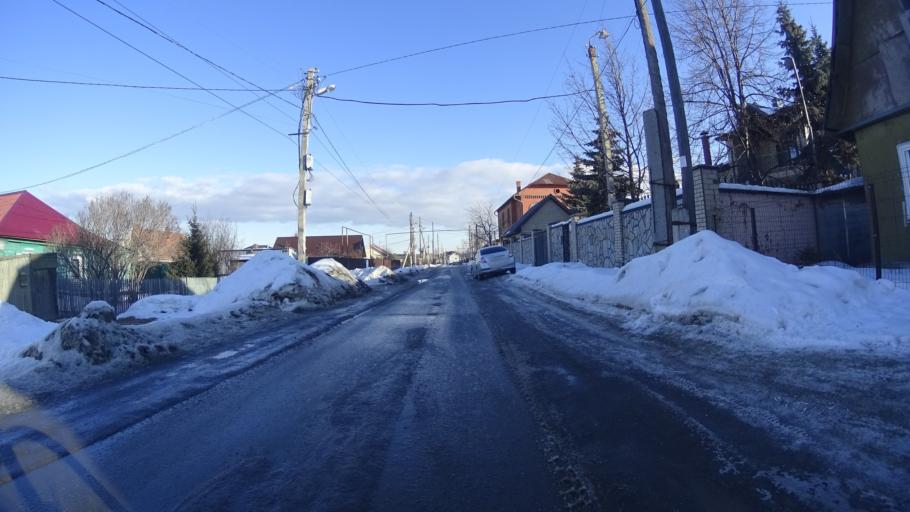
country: RU
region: Chelyabinsk
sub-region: Gorod Chelyabinsk
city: Chelyabinsk
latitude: 55.1551
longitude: 61.3074
